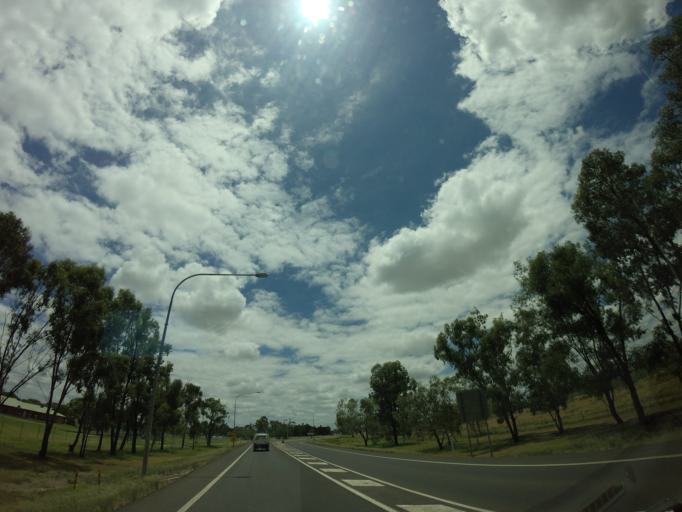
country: AU
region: Queensland
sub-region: Goondiwindi
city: Goondiwindi
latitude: -28.5543
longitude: 150.3209
